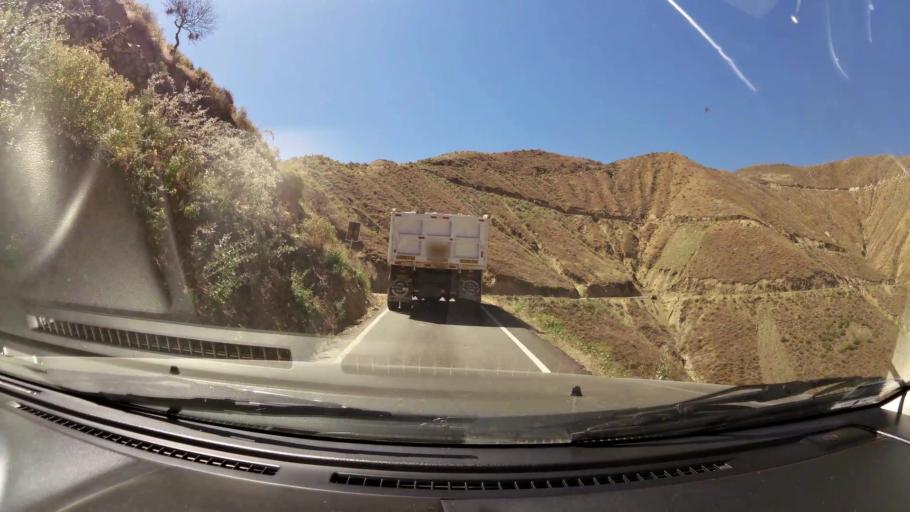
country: PE
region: Ica
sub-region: Provincia de Pisco
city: Huancano
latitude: -13.7251
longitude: -75.4586
